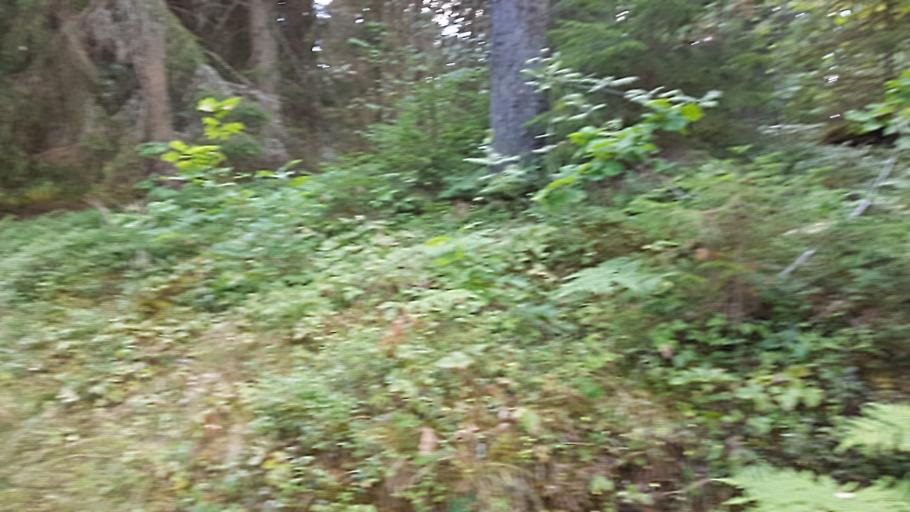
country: SE
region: Kalmar
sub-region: Vimmerby Kommun
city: Vimmerby
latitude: 57.6807
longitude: 15.8788
